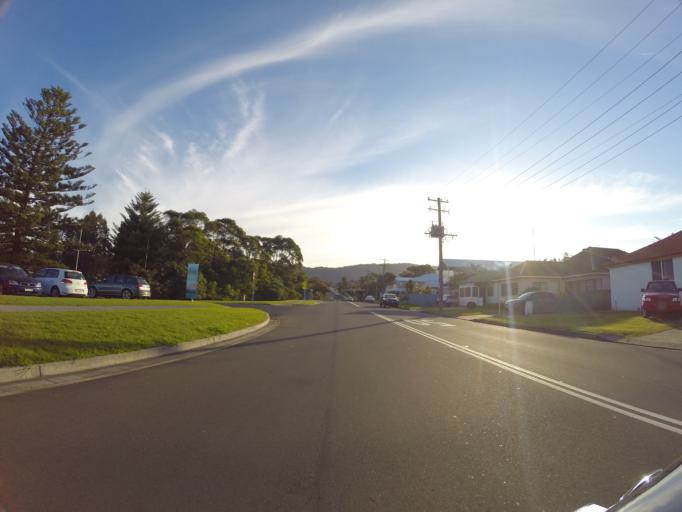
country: AU
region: New South Wales
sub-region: Wollongong
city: Bulli
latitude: -34.3398
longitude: 150.9235
